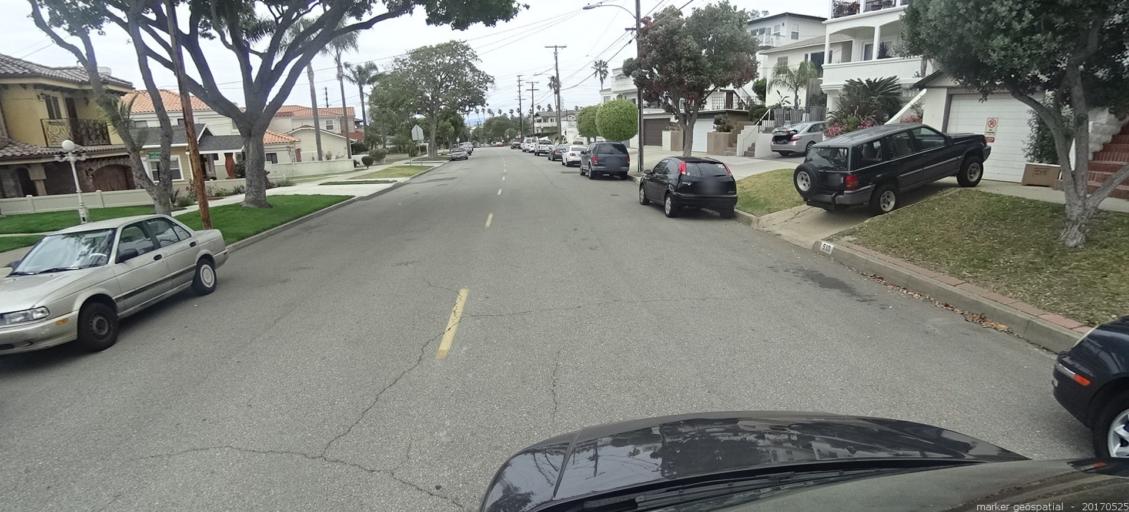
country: US
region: California
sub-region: Los Angeles County
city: Redondo Beach
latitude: 33.8472
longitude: -118.3855
